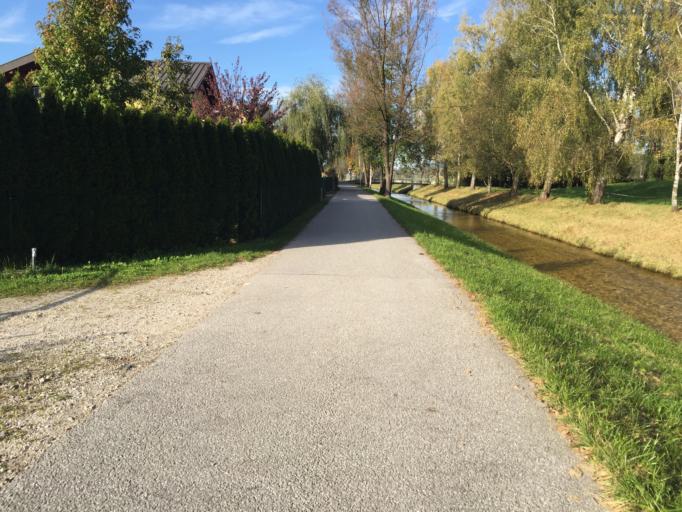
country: AT
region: Salzburg
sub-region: Politischer Bezirk Salzburg-Umgebung
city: Grodig
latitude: 47.7640
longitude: 13.0001
